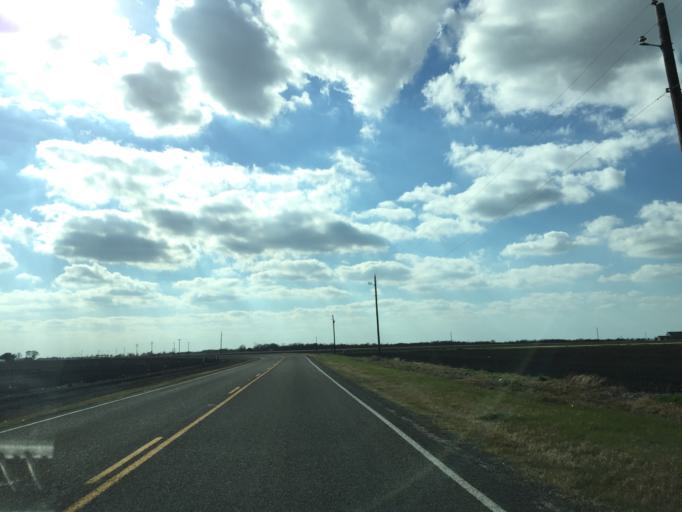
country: US
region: Texas
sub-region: Williamson County
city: Granger
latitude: 30.6738
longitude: -97.3499
